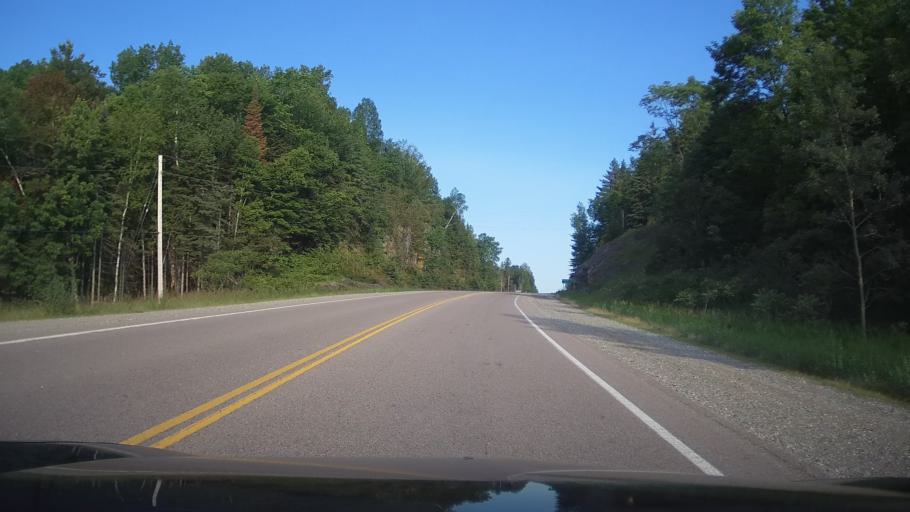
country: CA
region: Ontario
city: Skatepark
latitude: 44.7515
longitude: -76.8341
